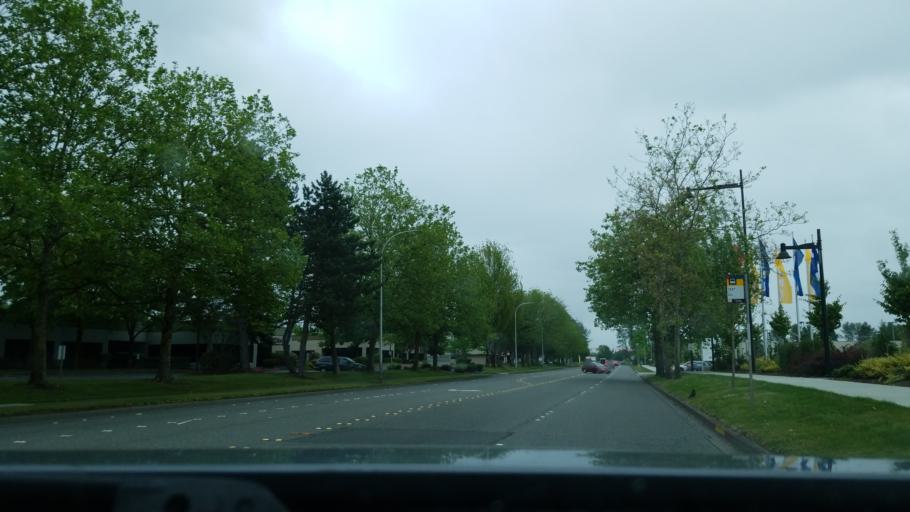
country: US
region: Washington
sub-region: King County
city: Renton
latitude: 47.4437
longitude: -122.2240
